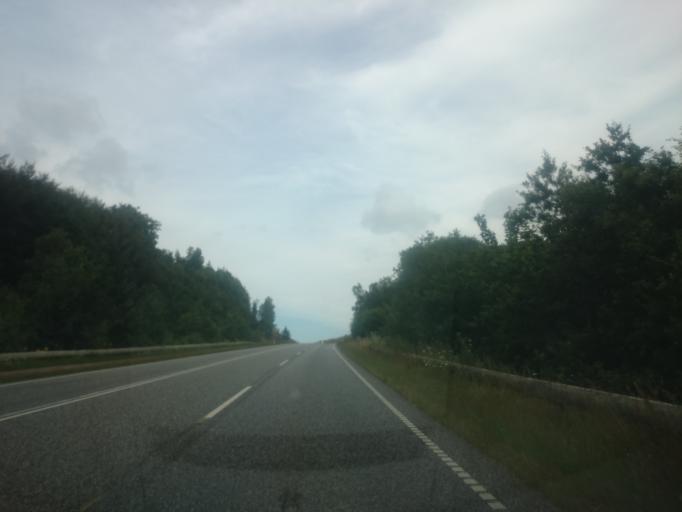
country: DK
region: South Denmark
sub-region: Vejle Kommune
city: Jelling
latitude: 55.6877
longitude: 9.3801
